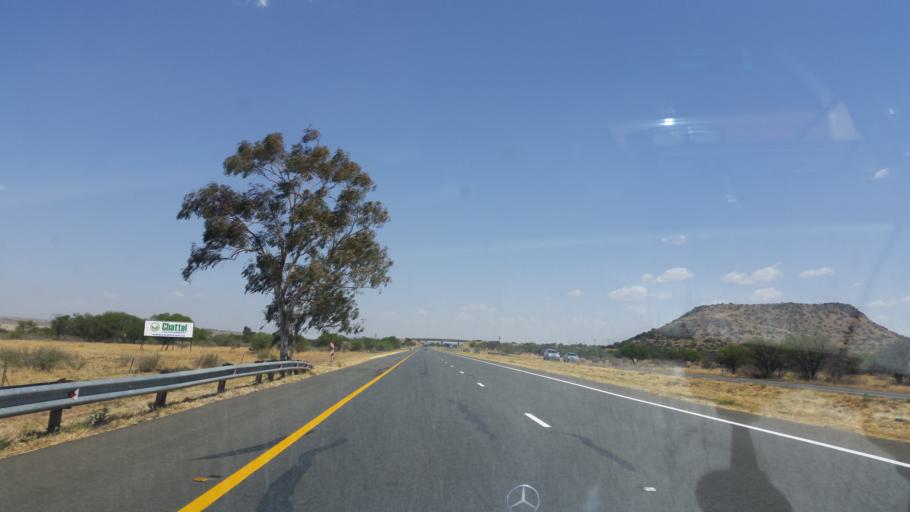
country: ZA
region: Orange Free State
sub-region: Mangaung Metropolitan Municipality
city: Bloemfontein
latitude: -28.9483
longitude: 26.3992
